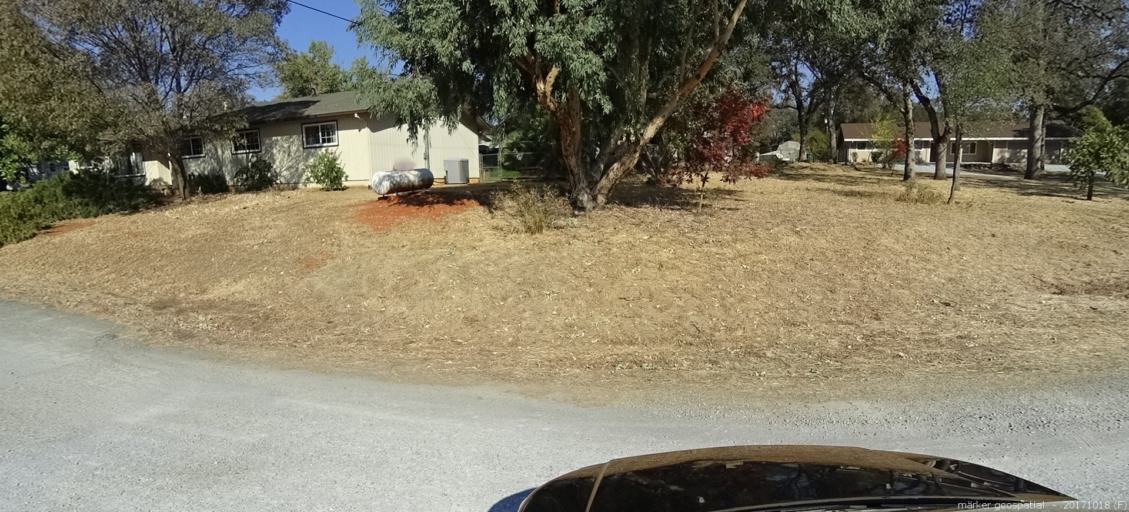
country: US
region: California
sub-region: Shasta County
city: Palo Cedro
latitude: 40.5472
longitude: -122.3001
